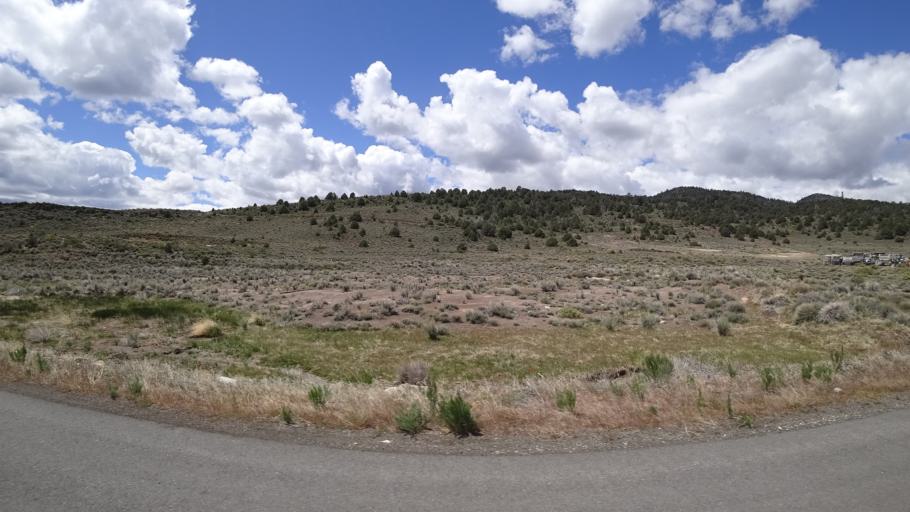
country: US
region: California
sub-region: Mono County
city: Bridgeport
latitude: 38.2753
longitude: -119.2882
